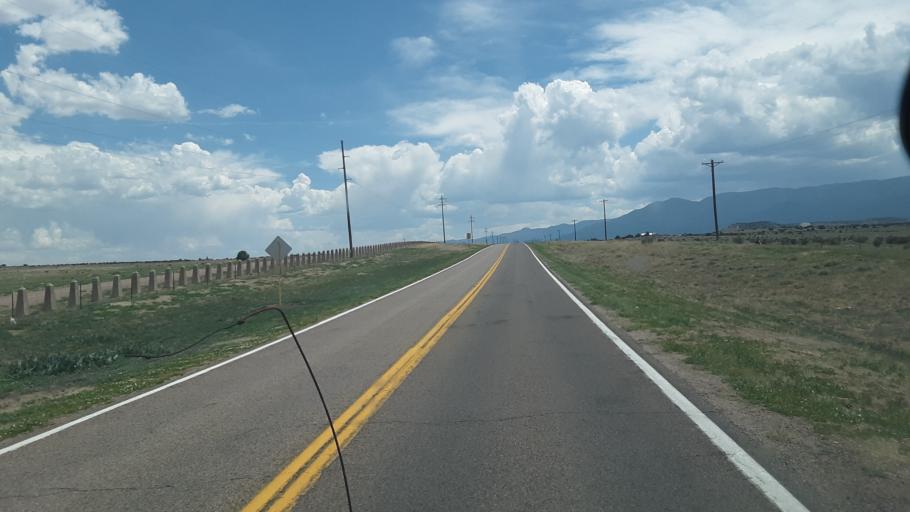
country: US
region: Colorado
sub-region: Fremont County
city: Florence
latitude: 38.3591
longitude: -105.1072
